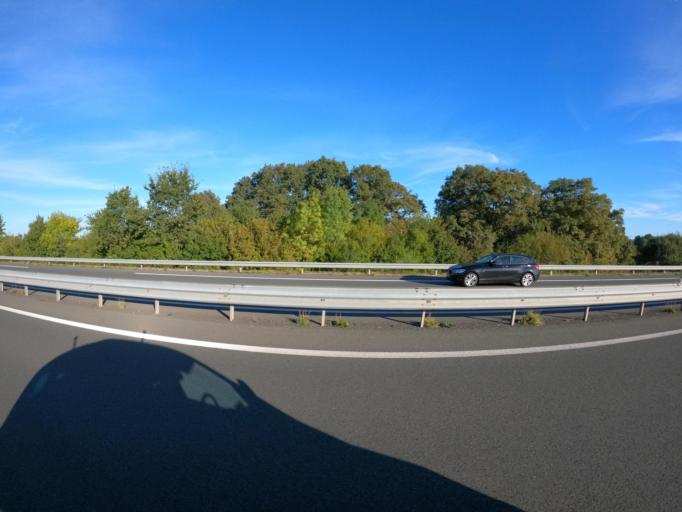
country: FR
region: Pays de la Loire
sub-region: Departement de Maine-et-Loire
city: Chemille-Melay
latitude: 47.1952
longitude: -0.7744
